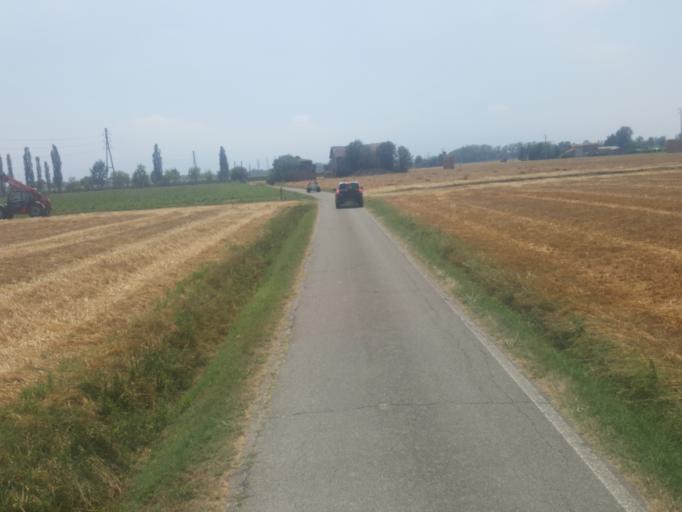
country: IT
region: Emilia-Romagna
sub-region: Provincia di Modena
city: Gaggio
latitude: 44.6431
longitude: 11.0000
